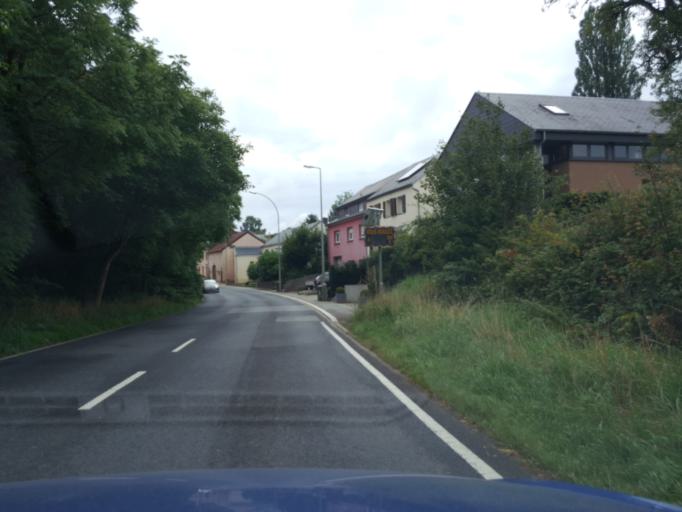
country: LU
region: Luxembourg
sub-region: Canton de Capellen
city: Kopstal
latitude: 49.6973
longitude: 6.0717
